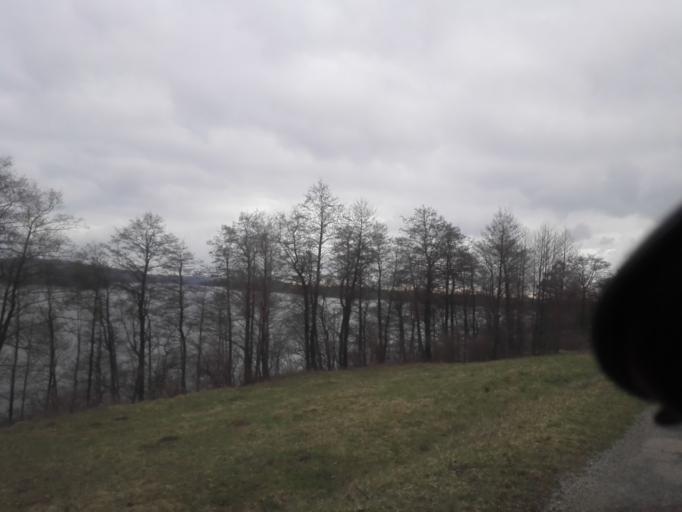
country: PL
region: Podlasie
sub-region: Suwalki
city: Suwalki
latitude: 54.2417
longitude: 22.9826
